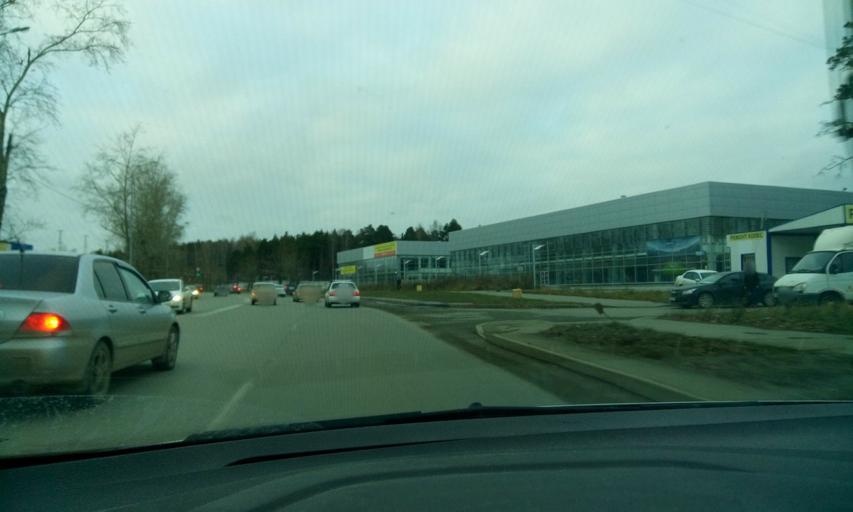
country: RU
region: Sverdlovsk
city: Yekaterinburg
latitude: 56.9113
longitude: 60.6196
